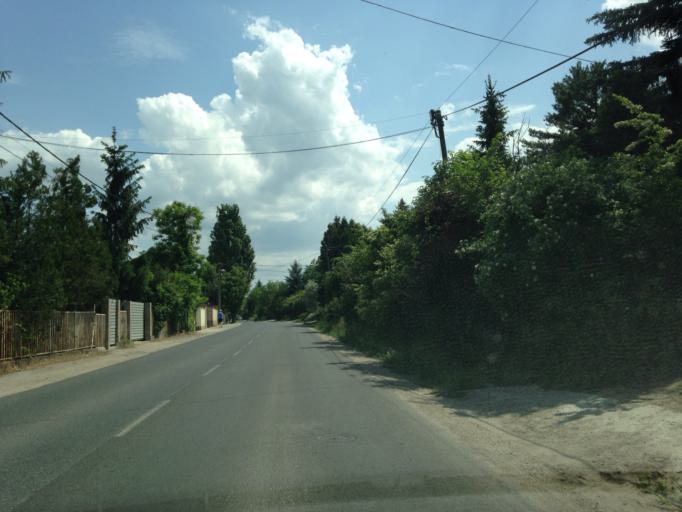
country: HU
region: Pest
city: Szentendre
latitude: 47.6802
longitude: 19.0641
